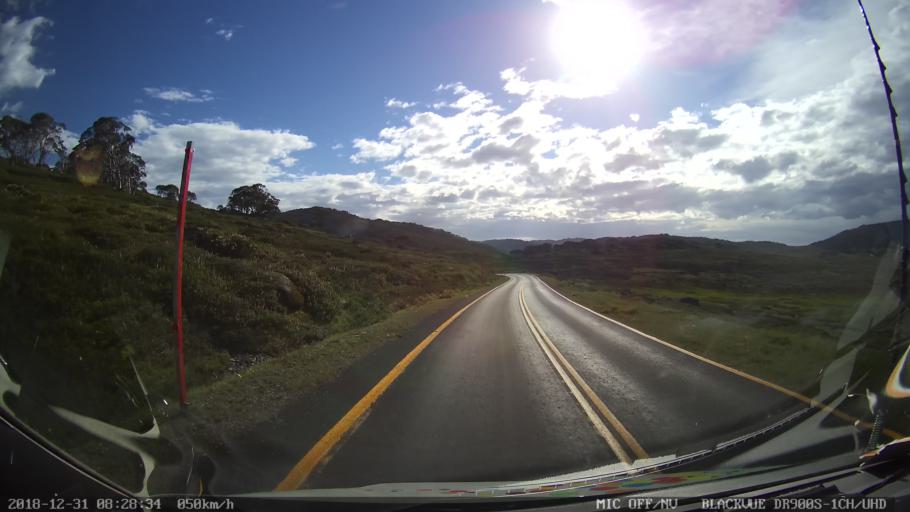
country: AU
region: New South Wales
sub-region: Snowy River
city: Jindabyne
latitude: -36.4277
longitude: 148.3470
